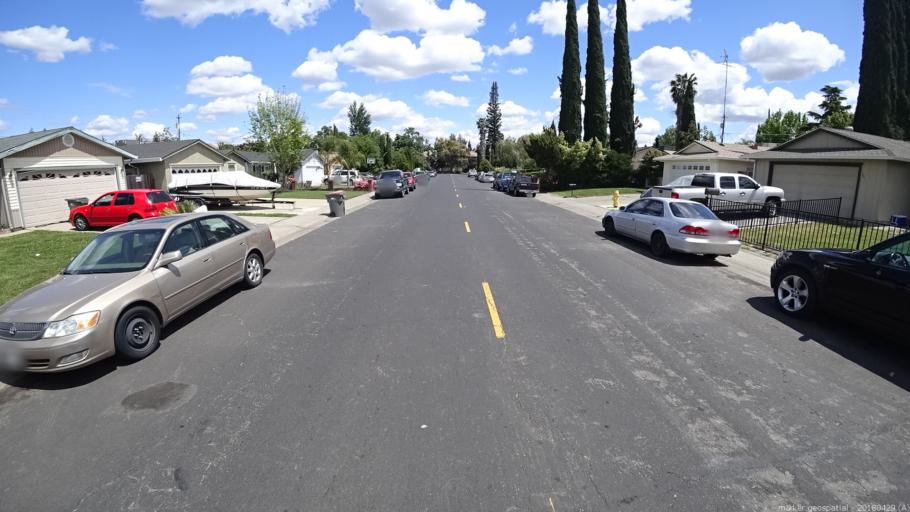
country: US
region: California
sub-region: Yolo County
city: West Sacramento
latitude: 38.5998
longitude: -121.5278
